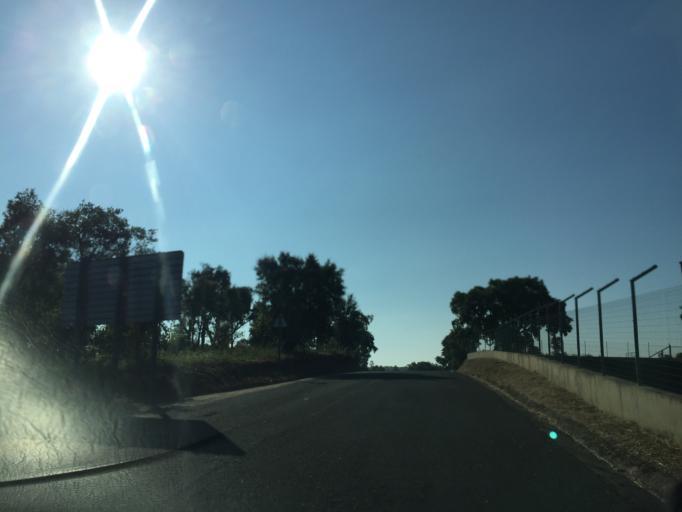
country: PT
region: Santarem
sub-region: Abrantes
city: Alferrarede
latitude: 39.5250
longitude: -8.1539
